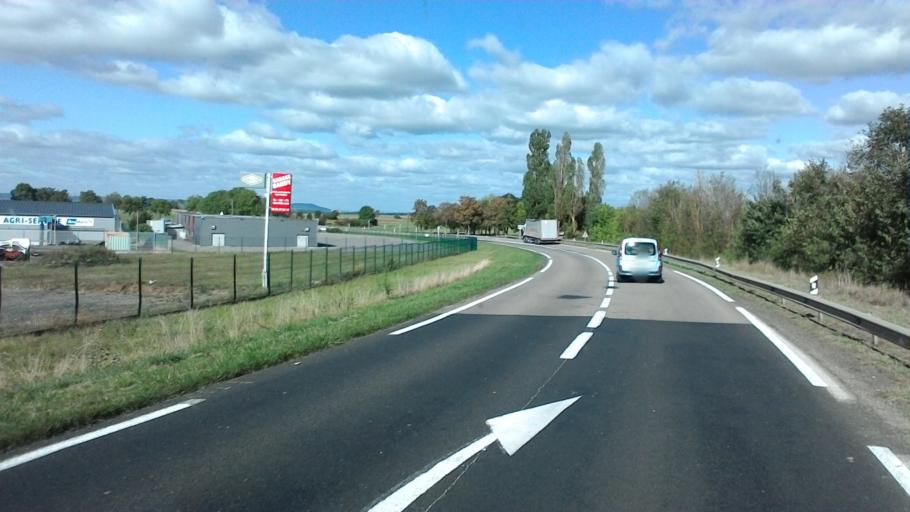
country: FR
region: Lorraine
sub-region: Departement de Meurthe-et-Moselle
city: Colombey-les-Belles
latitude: 48.5495
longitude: 5.8966
